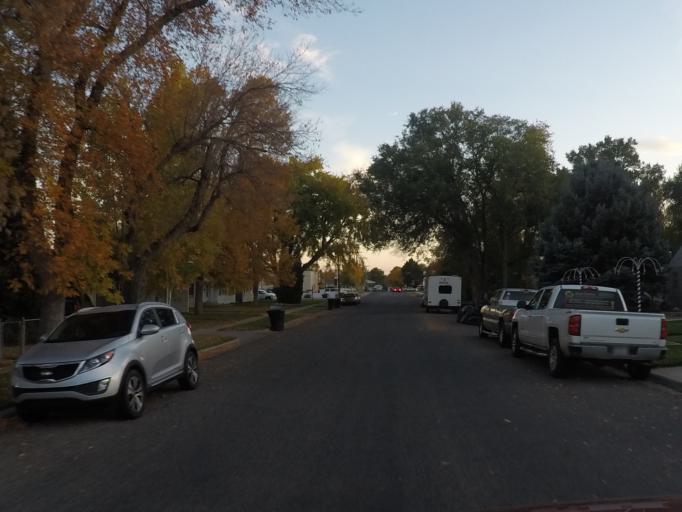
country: US
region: Montana
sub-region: Yellowstone County
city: Billings
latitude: 45.7858
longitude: -108.5436
